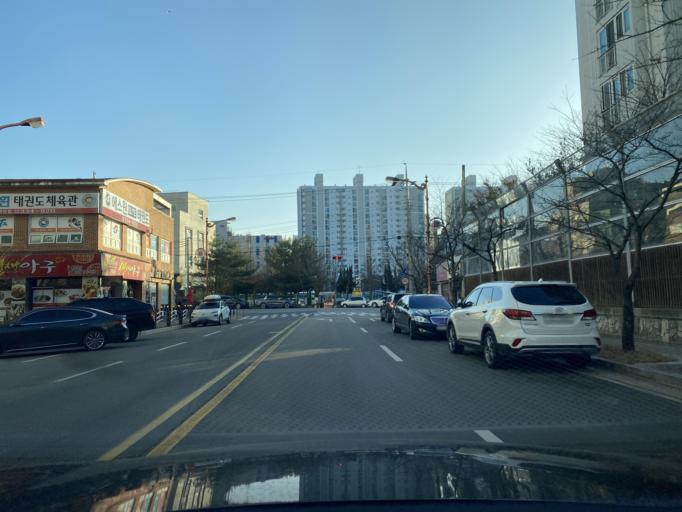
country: KR
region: Chungcheongnam-do
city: Yesan
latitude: 36.6954
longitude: 126.8331
